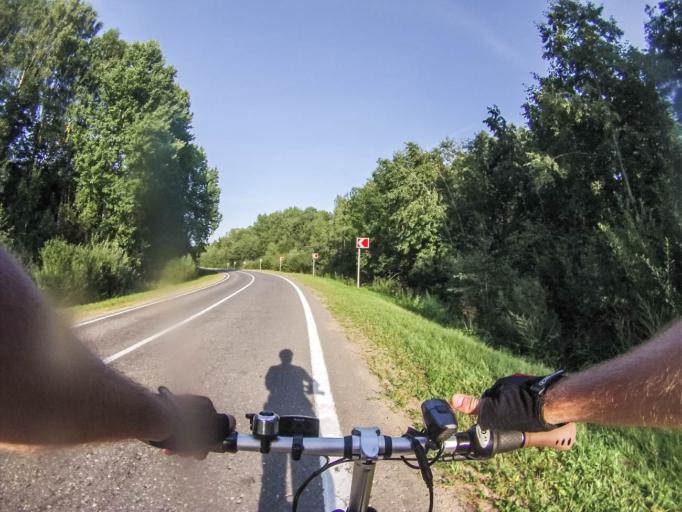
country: RU
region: Jaroslavl
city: Myshkin
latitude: 57.7151
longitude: 38.4010
